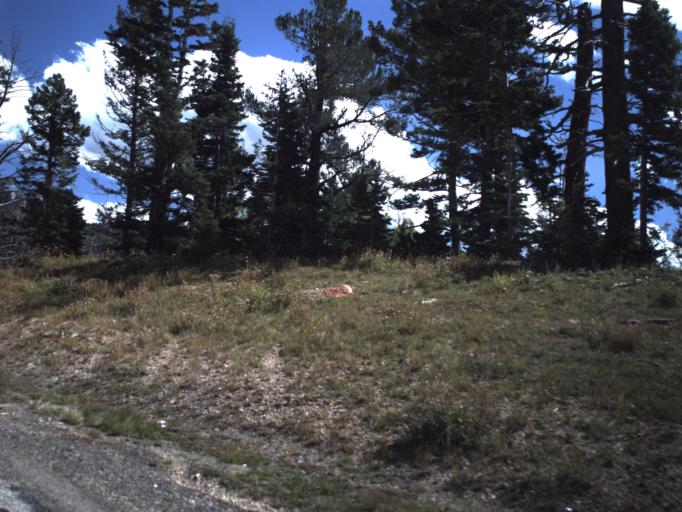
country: US
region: Utah
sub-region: Iron County
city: Cedar City
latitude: 37.5813
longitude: -112.8749
